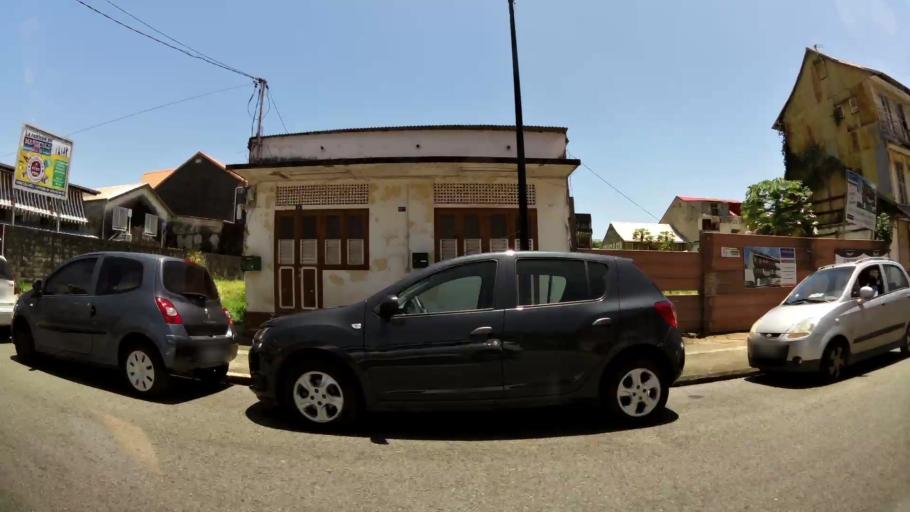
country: GF
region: Guyane
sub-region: Guyane
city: Cayenne
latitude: 4.9414
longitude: -52.3320
